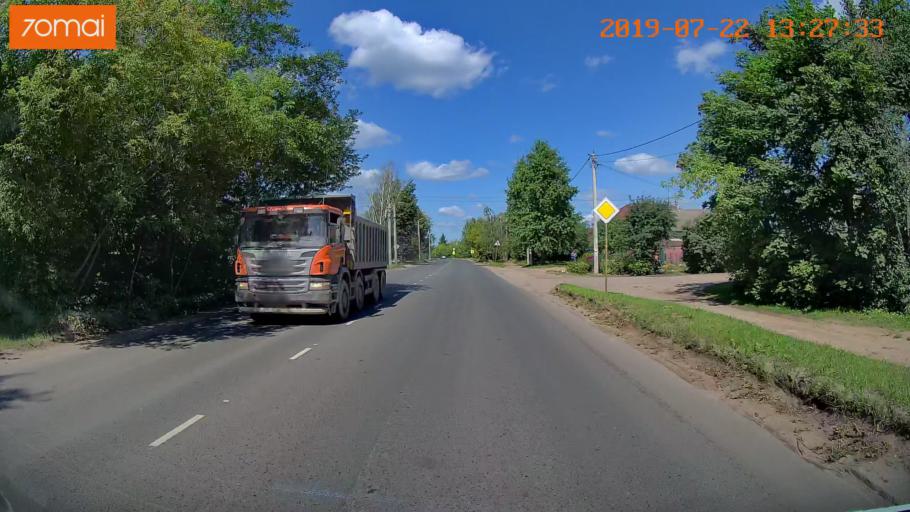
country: RU
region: Ivanovo
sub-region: Gorod Ivanovo
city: Ivanovo
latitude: 57.0359
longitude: 40.9504
